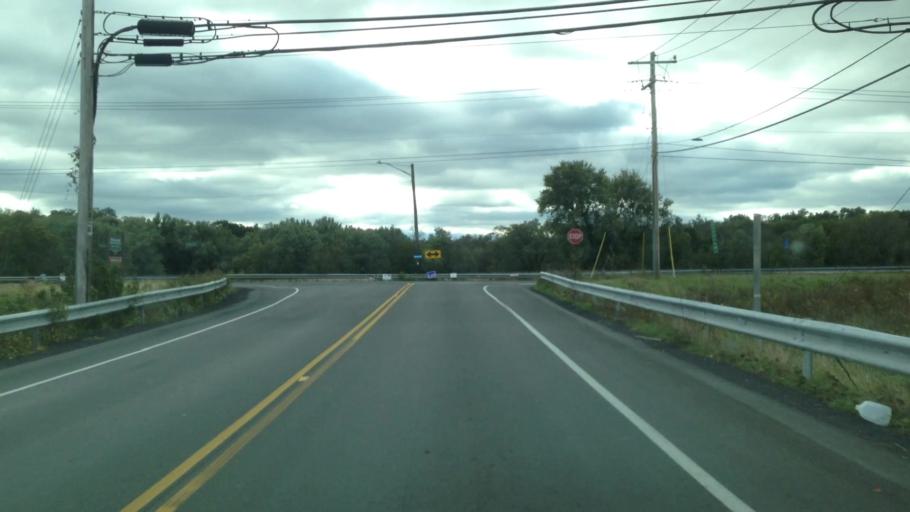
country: US
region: New York
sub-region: Ulster County
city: New Paltz
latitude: 41.7476
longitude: -74.0928
